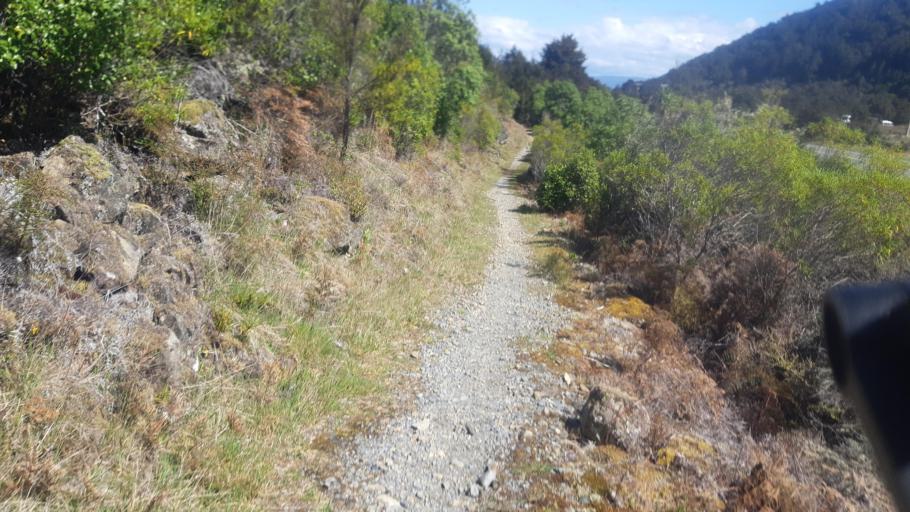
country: NZ
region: Tasman
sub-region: Tasman District
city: Wakefield
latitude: -41.7952
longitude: 172.8360
